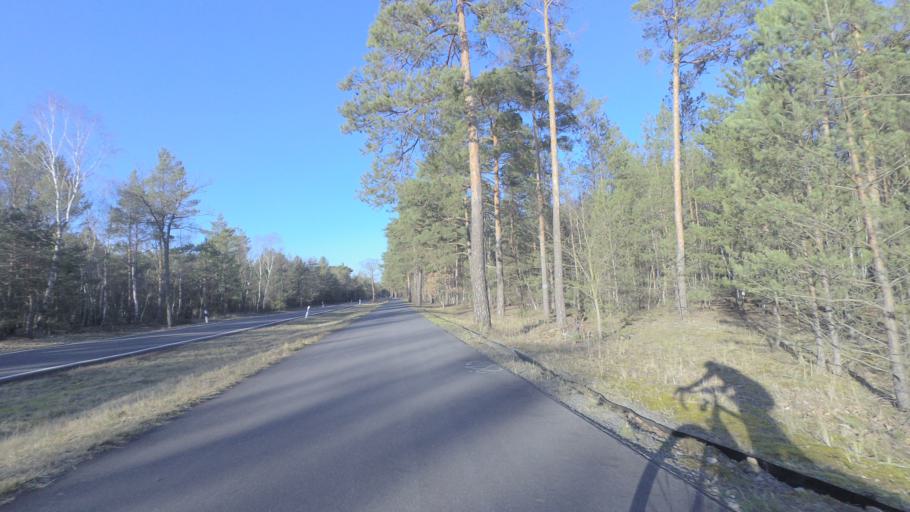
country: DE
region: Brandenburg
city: Sperenberg
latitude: 52.0263
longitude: 13.3185
